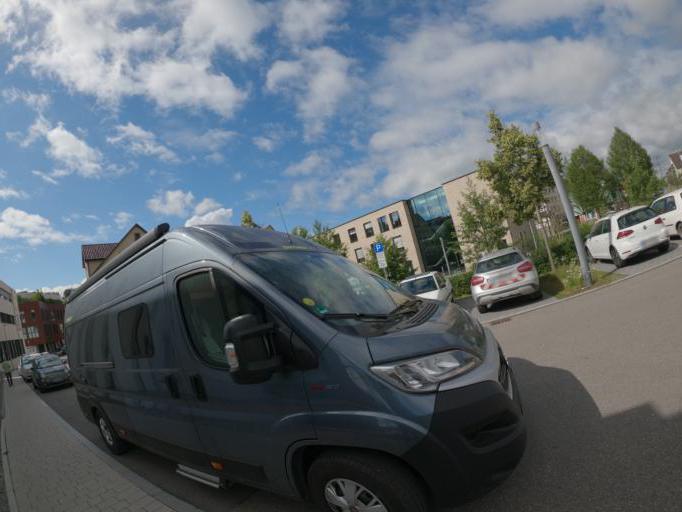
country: DE
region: Baden-Wuerttemberg
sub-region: Regierungsbezirk Stuttgart
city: Ebersbach an der Fils
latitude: 48.7152
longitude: 9.5239
